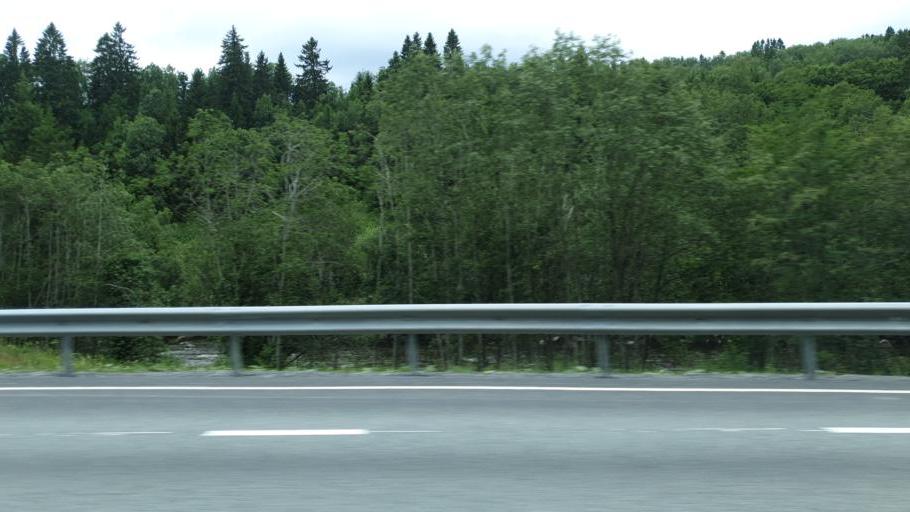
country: NO
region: Sor-Trondelag
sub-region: Midtre Gauldal
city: Storen
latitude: 62.9807
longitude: 10.2346
